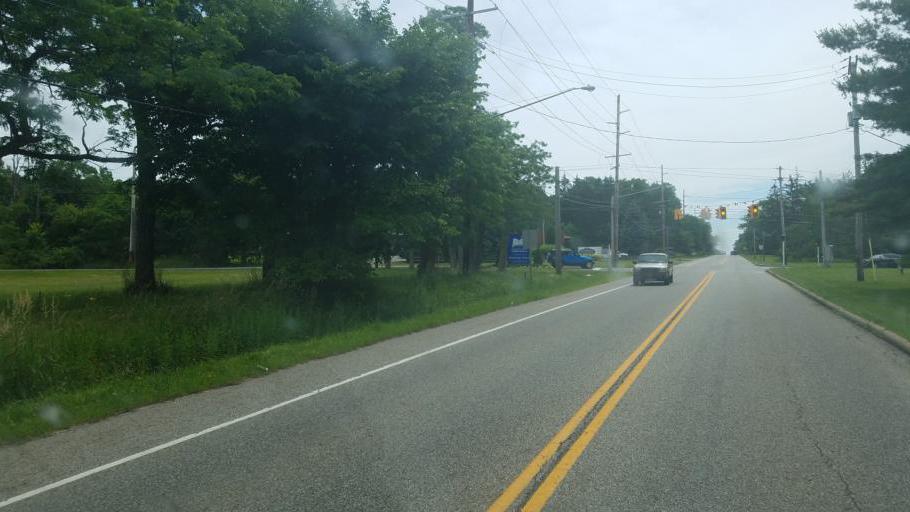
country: US
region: Ohio
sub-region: Geauga County
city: Bainbridge
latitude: 41.4001
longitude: -81.3088
